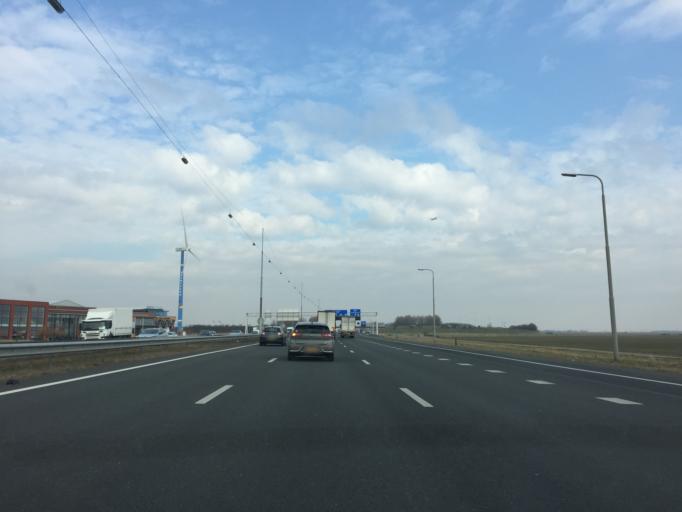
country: NL
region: North Holland
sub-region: Gemeente Uitgeest
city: Uitgeest
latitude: 52.5024
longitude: 4.7023
